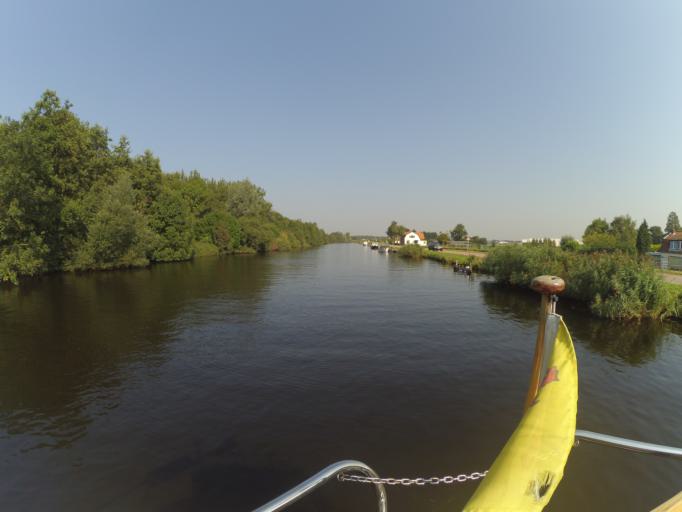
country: NL
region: North Holland
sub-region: Gemeente Bloemendaal
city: Bennebroek
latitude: 52.3206
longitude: 4.6118
